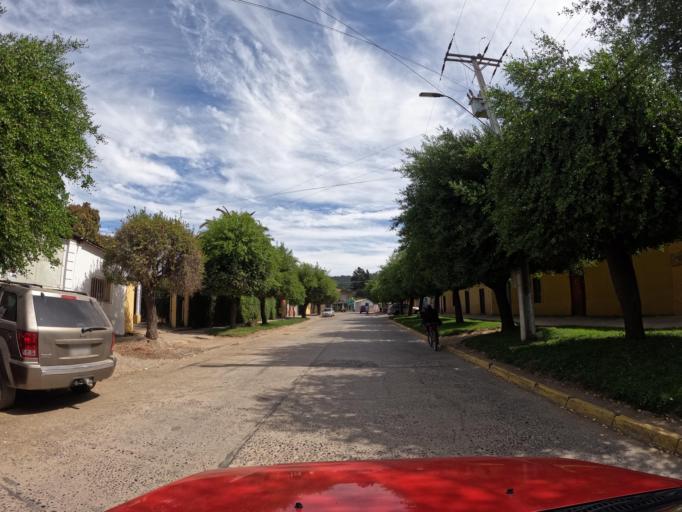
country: CL
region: Maule
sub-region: Provincia de Talca
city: Constitucion
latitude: -35.0901
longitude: -72.0217
